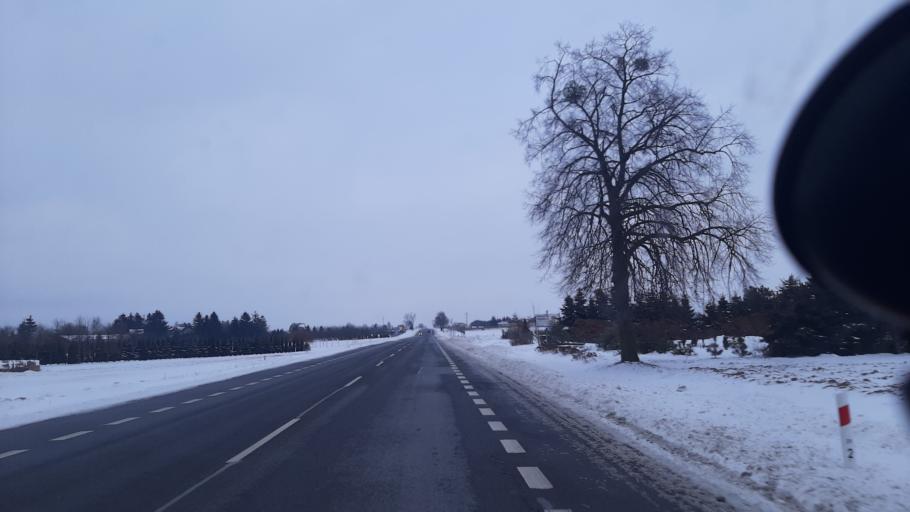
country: PL
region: Lublin Voivodeship
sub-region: Powiat pulawski
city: Kurow
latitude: 51.3843
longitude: 22.2167
